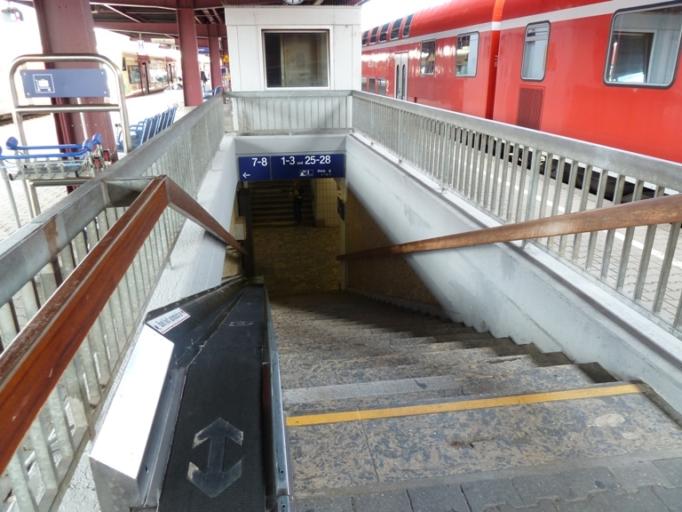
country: DE
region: Baden-Wuerttemberg
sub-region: Tuebingen Region
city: Ulm
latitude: 48.3993
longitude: 9.9825
